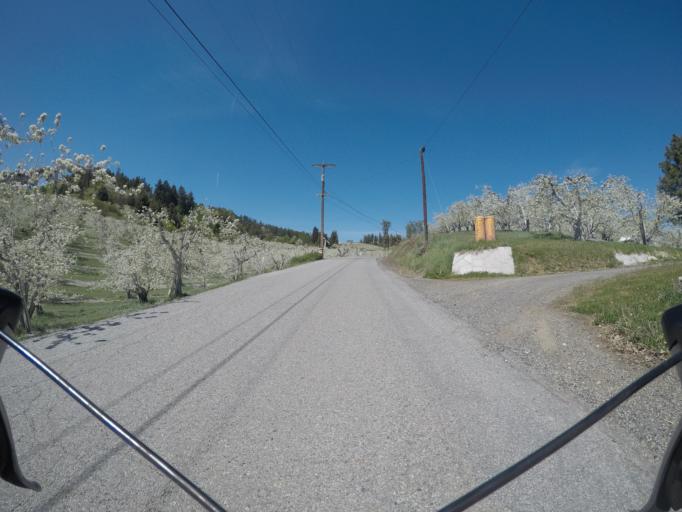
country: US
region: Washington
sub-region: Chelan County
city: Cashmere
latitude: 47.5380
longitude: -120.5676
